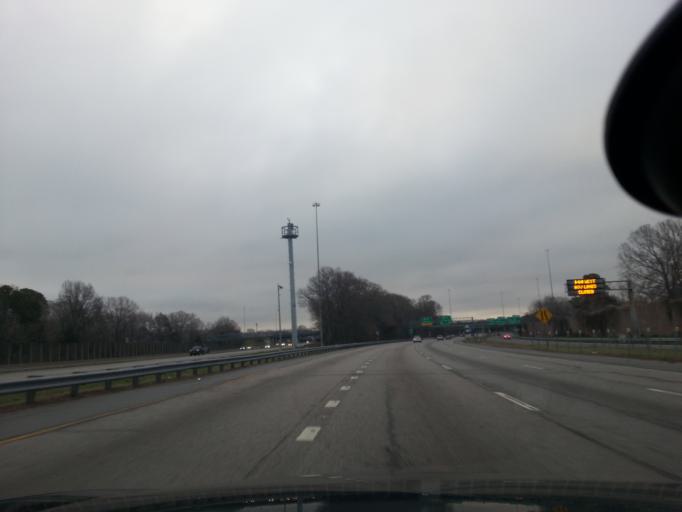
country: US
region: Virginia
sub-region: City of Chesapeake
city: Chesapeake
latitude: 36.8447
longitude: -76.2046
